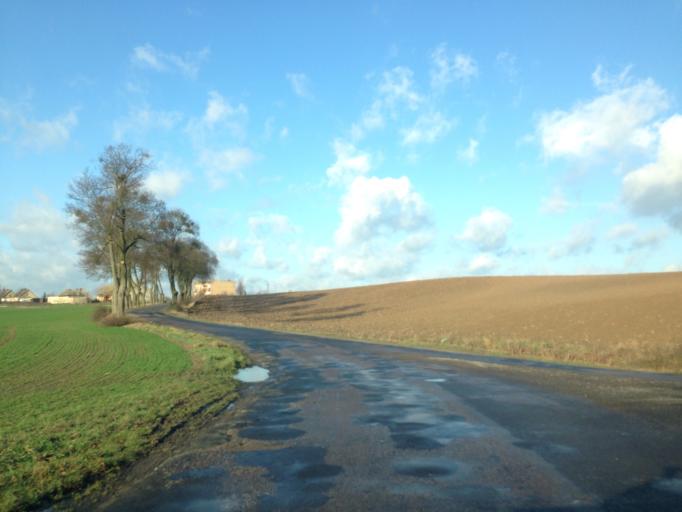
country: PL
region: Kujawsko-Pomorskie
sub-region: Powiat grudziadzki
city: Lasin
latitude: 53.4900
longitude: 19.0937
